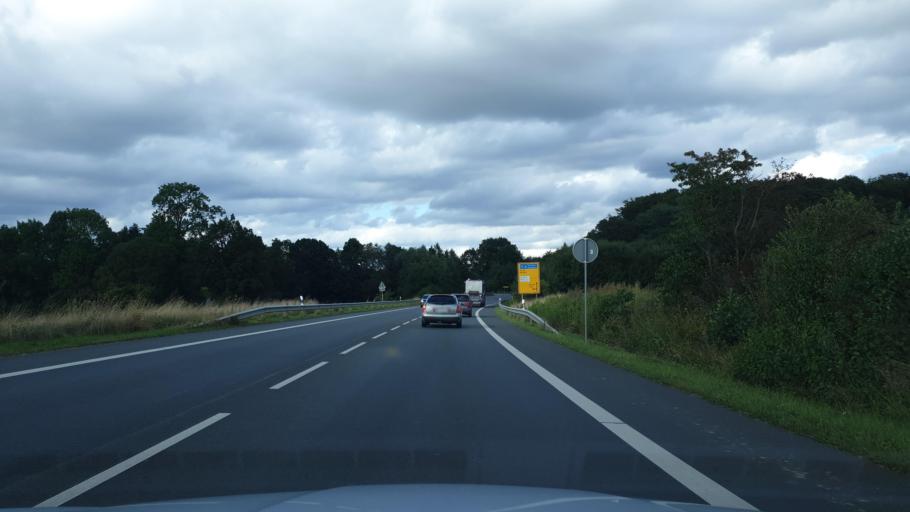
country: DE
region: North Rhine-Westphalia
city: Enger
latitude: 52.1260
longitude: 8.5598
